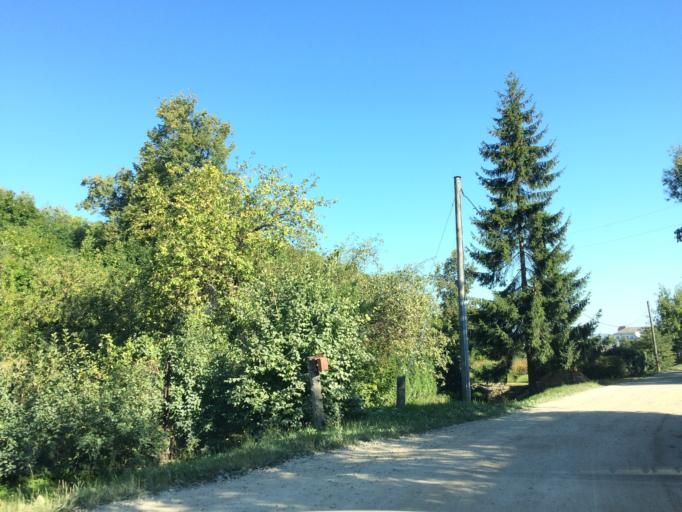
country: LV
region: Rezekne
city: Rezekne
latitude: 56.4962
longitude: 27.3278
